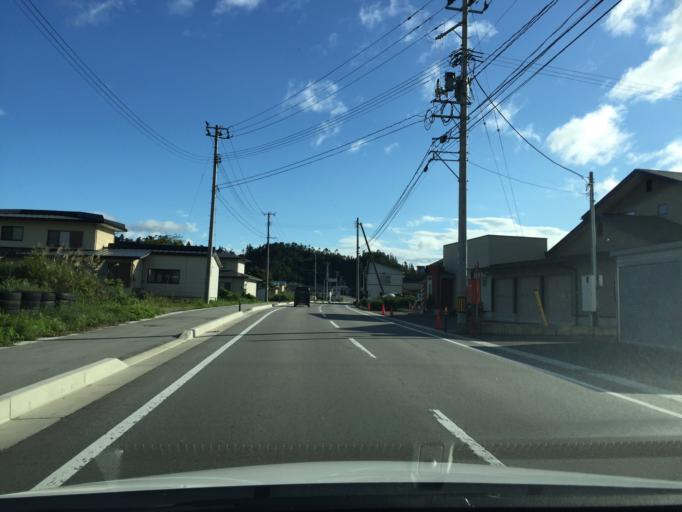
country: JP
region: Yamagata
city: Yonezawa
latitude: 37.9386
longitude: 140.1679
